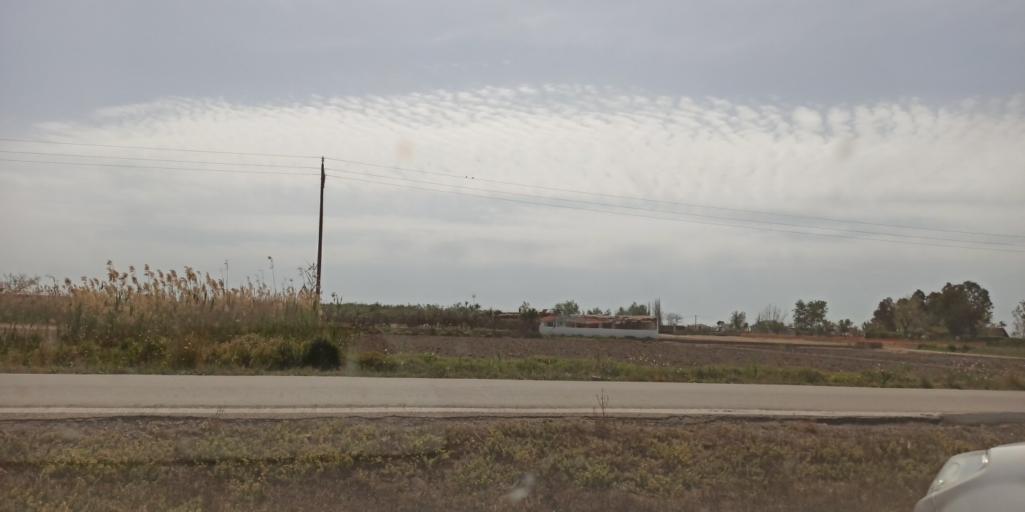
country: ES
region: Catalonia
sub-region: Provincia de Tarragona
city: Deltebre
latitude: 40.6443
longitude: 0.6870
